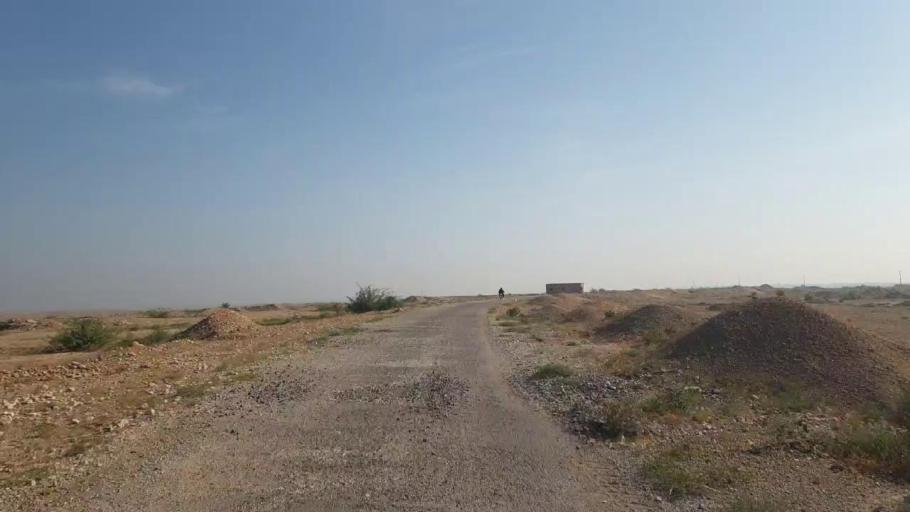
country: PK
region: Sindh
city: Matiari
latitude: 25.6227
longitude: 68.3063
